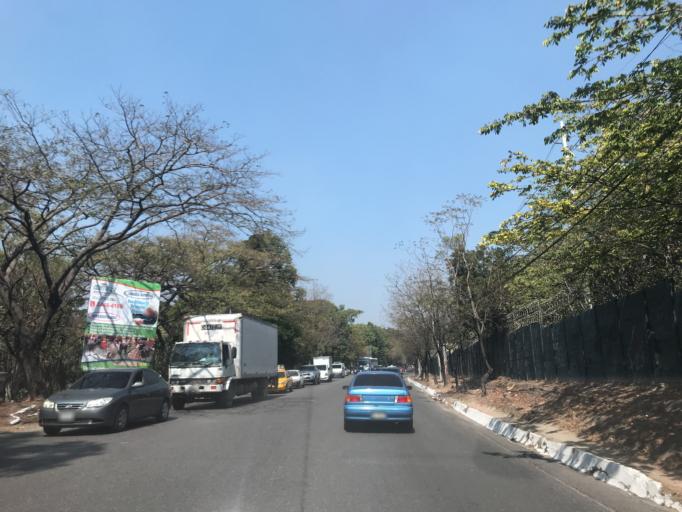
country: GT
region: Guatemala
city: Petapa
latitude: 14.5342
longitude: -90.5565
